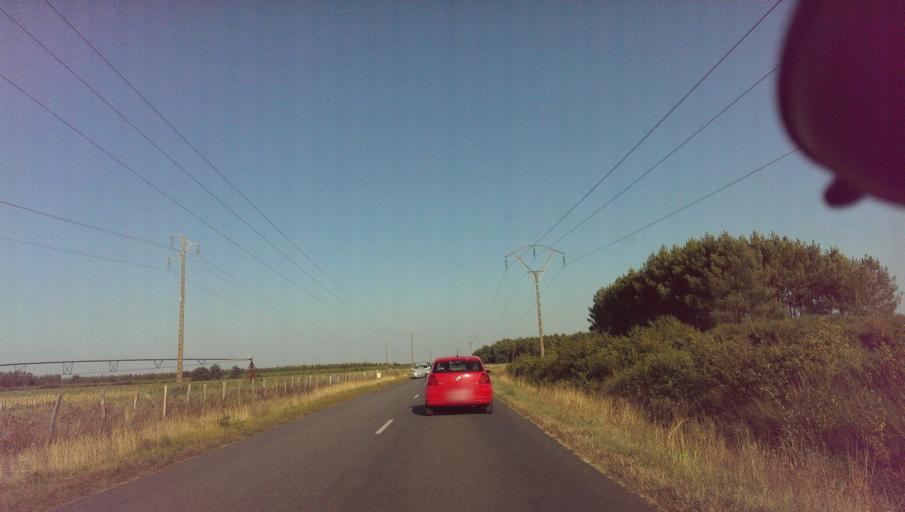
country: FR
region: Aquitaine
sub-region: Departement des Landes
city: Mimizan
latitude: 44.1865
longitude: -1.2017
